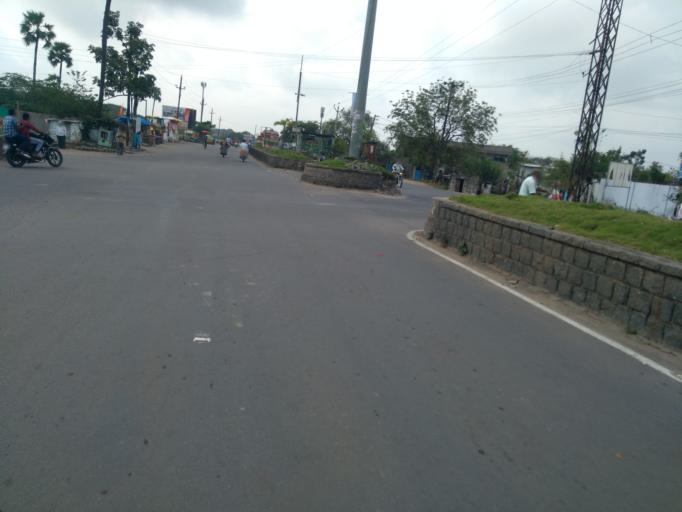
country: IN
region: Telangana
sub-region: Warangal
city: Warangal
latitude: 17.9602
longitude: 79.6010
